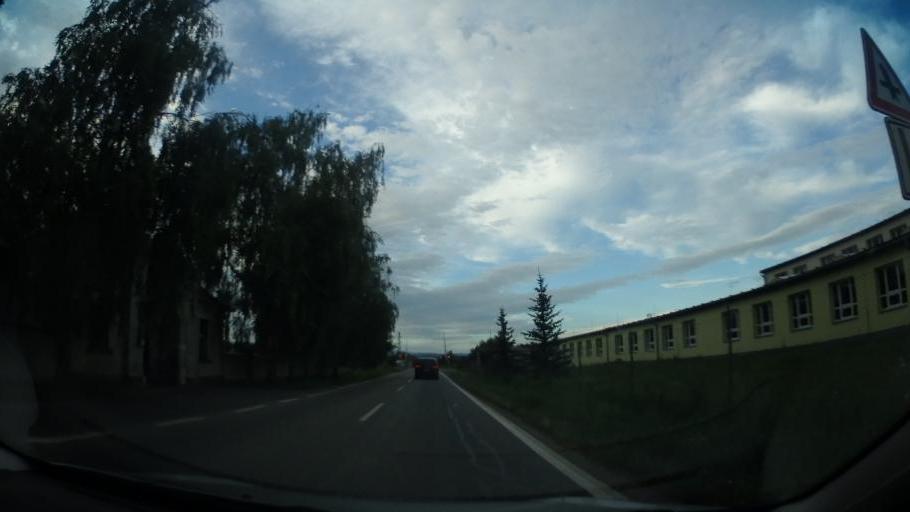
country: CZ
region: Olomoucky
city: Cervenka
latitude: 49.7262
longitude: 17.0810
